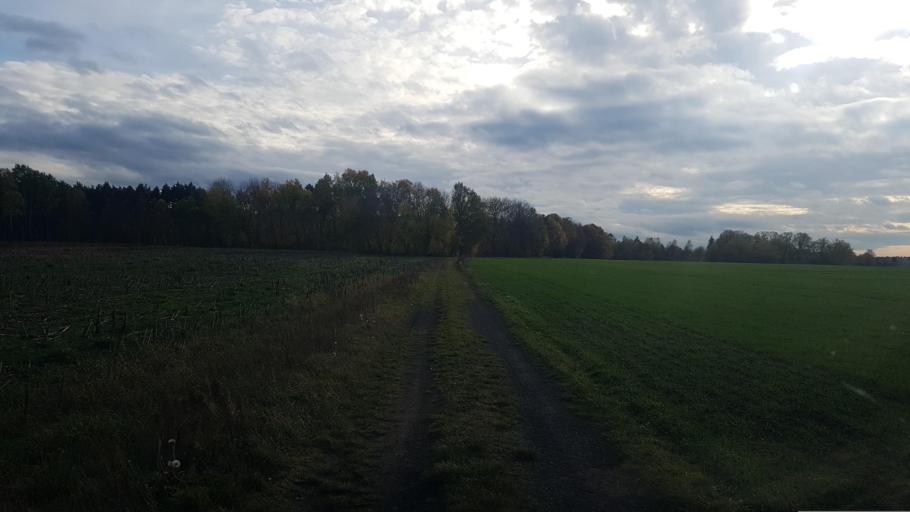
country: DE
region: Brandenburg
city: Wiesenburg
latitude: 52.0789
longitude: 12.4636
